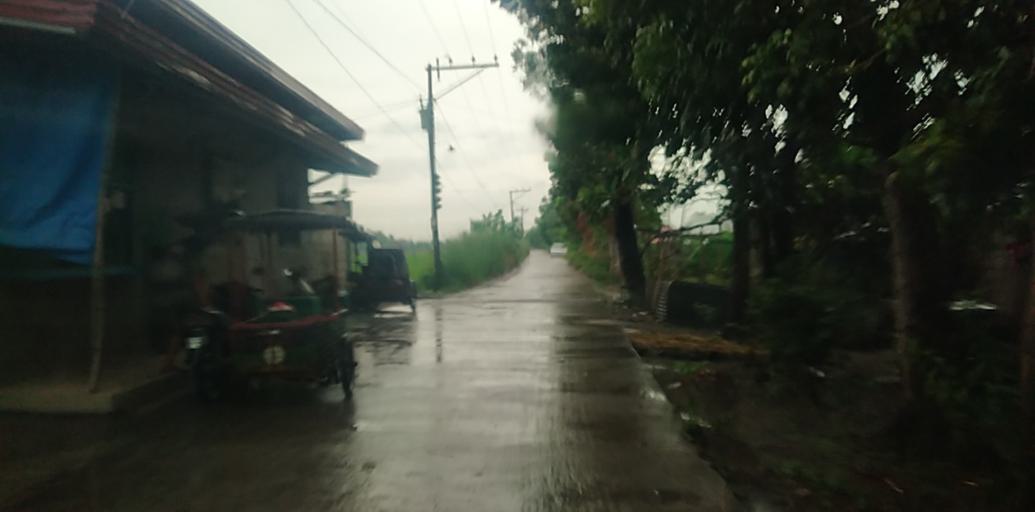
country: PH
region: Central Luzon
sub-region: Province of Pampanga
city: Panlinlang
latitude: 15.1583
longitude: 120.7200
